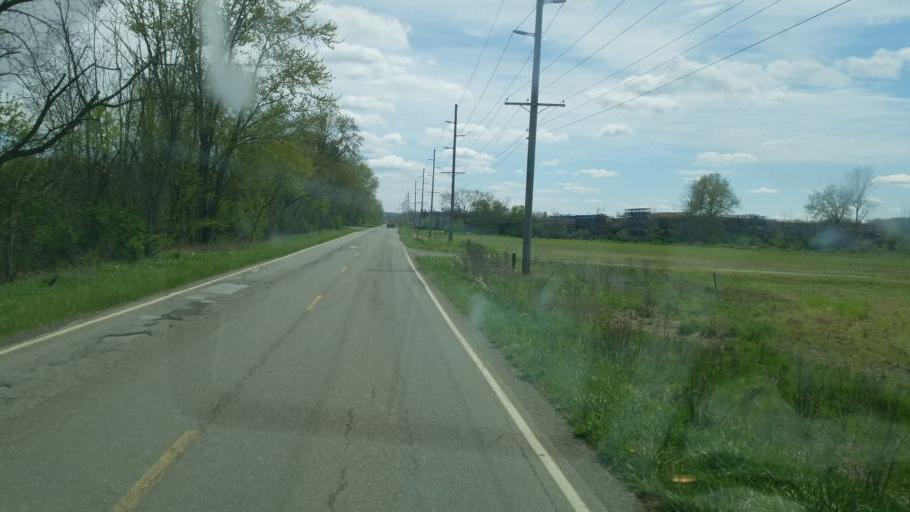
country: US
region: Ohio
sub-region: Wayne County
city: Wooster
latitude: 40.7752
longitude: -81.9443
